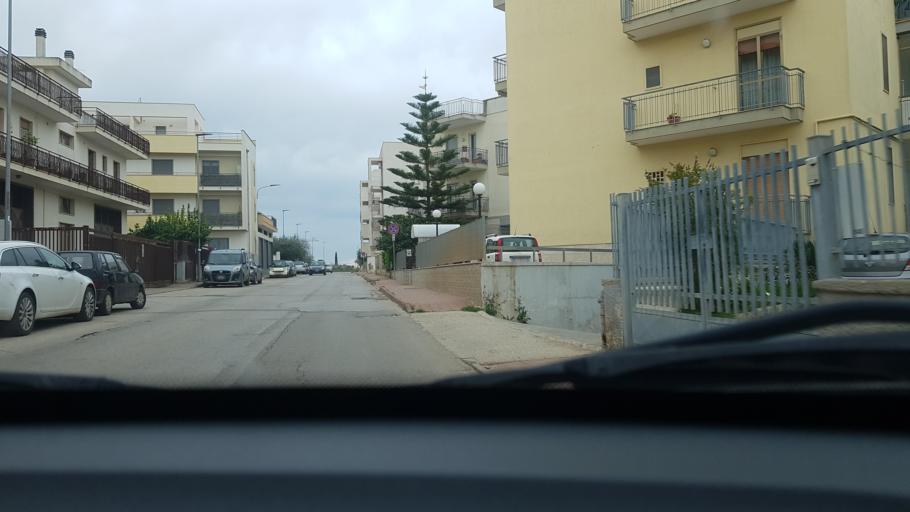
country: IT
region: Apulia
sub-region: Provincia di Bari
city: Noicattaro
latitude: 41.0325
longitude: 16.9806
